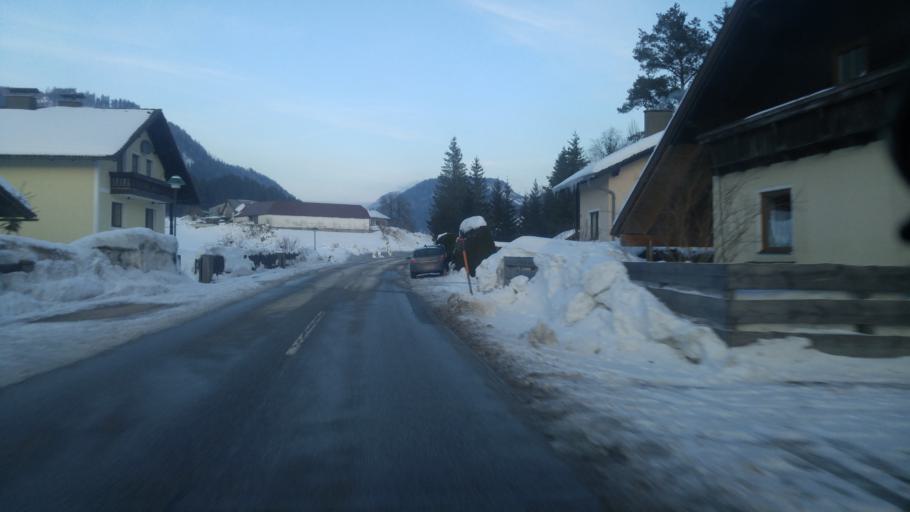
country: AT
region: Lower Austria
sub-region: Politischer Bezirk Wiener Neustadt
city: Rohr im Gebirge
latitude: 47.8901
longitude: 15.7197
